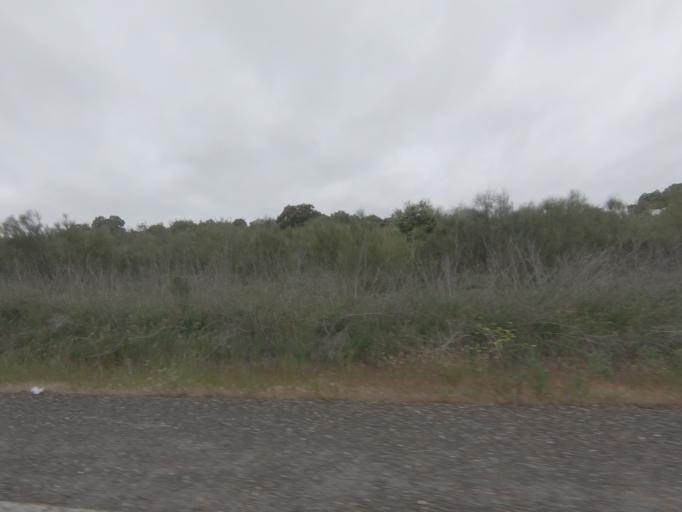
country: ES
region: Extremadura
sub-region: Provincia de Badajoz
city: La Roca de la Sierra
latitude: 39.1146
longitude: -6.6866
